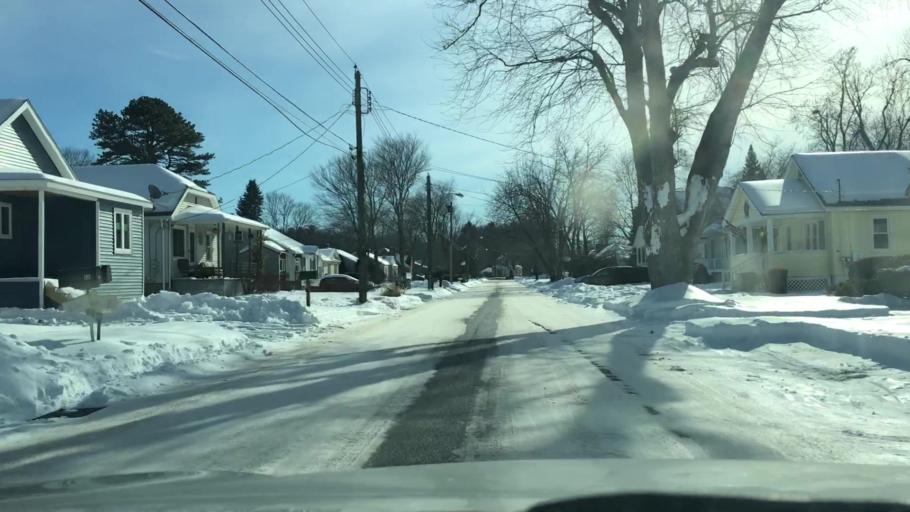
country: US
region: Massachusetts
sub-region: Hampden County
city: Agawam
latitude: 42.0728
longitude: -72.6558
